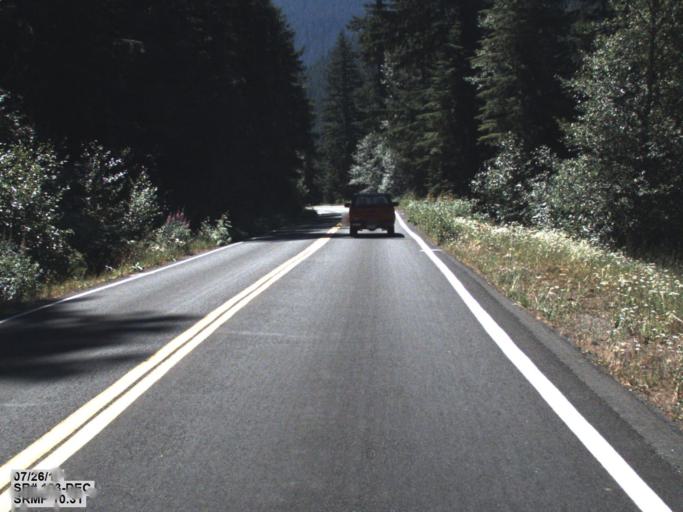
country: US
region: Washington
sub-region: King County
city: Enumclaw
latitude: 46.8212
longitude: -121.5493
